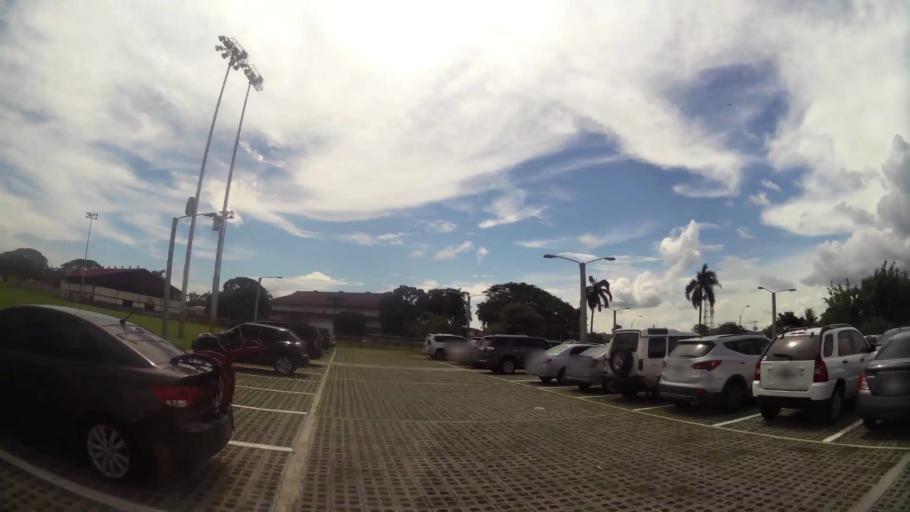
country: PA
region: Panama
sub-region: Distrito de Panama
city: Ancon
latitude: 9.0021
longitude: -79.5816
